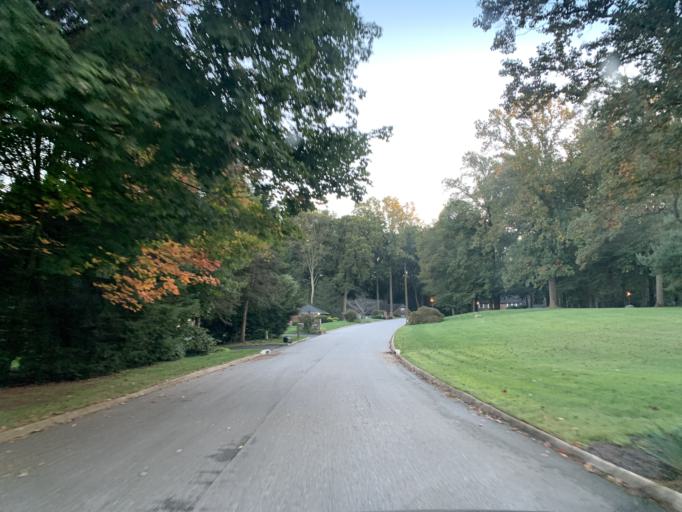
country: US
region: Maryland
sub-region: Harford County
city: Bel Air South
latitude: 39.5146
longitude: -76.2888
